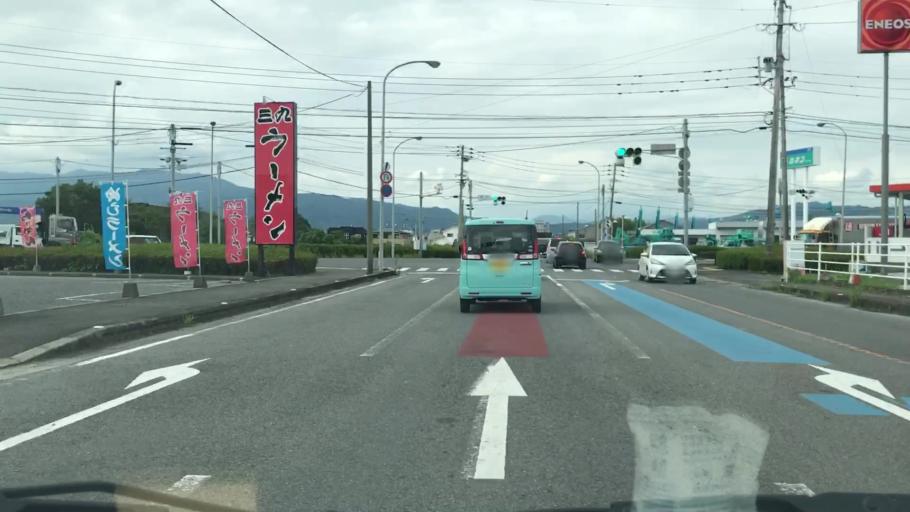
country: JP
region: Saga Prefecture
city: Saga-shi
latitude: 33.2684
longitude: 130.2617
